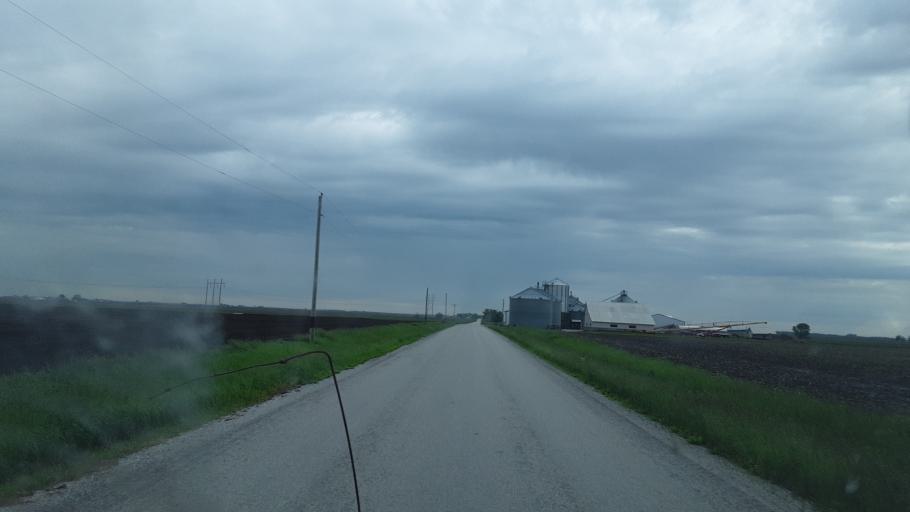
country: US
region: Illinois
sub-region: McDonough County
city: Macomb
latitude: 40.3813
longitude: -90.5303
